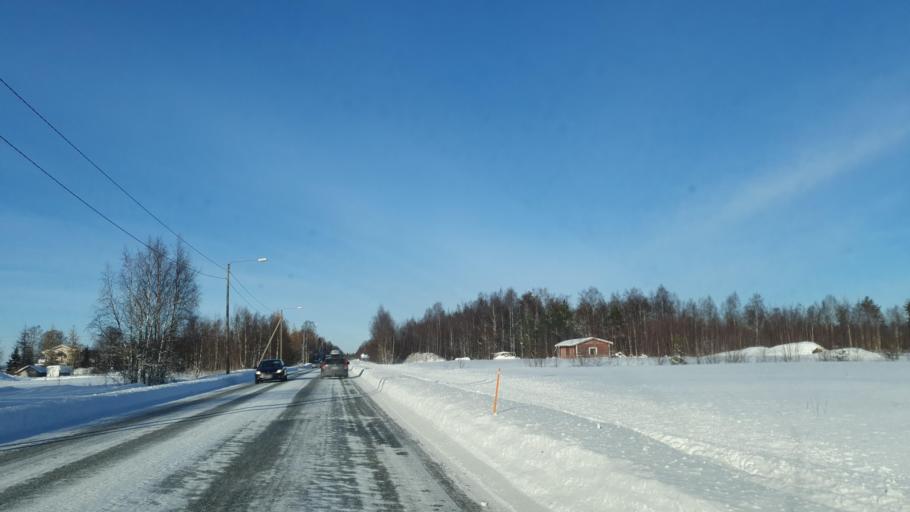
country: FI
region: Lapland
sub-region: Kemi-Tornio
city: Tornio
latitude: 66.0548
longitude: 24.0030
